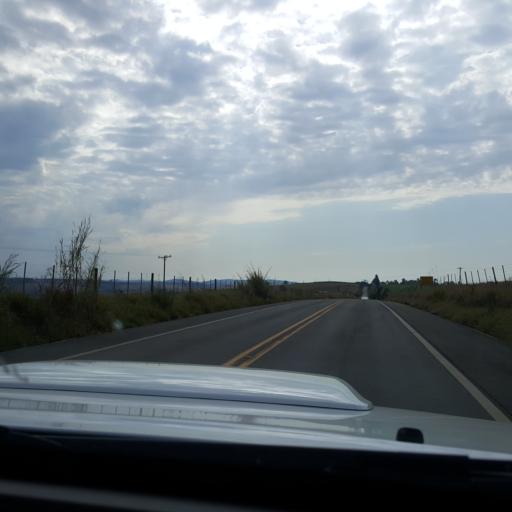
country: BR
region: Sao Paulo
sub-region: Itaporanga
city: Itaporanga
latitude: -23.7632
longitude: -49.4480
